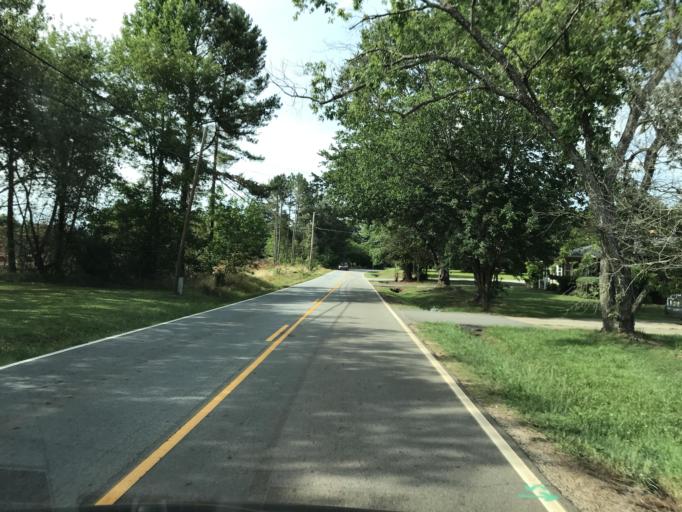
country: US
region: South Carolina
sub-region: Greenville County
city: Gantt
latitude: 34.7770
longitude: -82.4158
